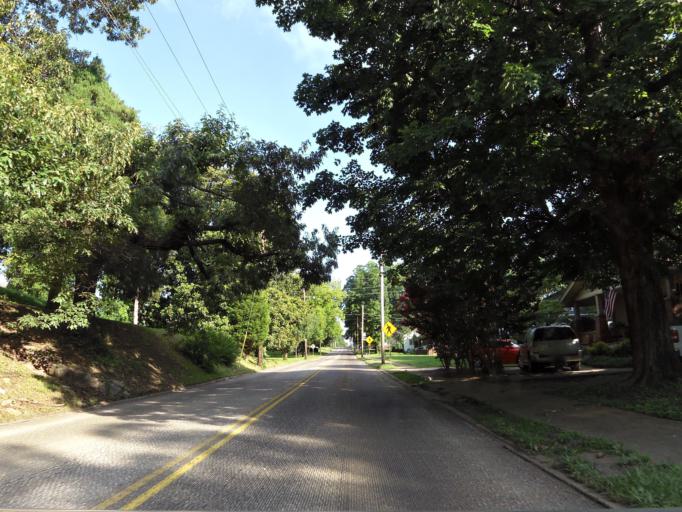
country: US
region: Tennessee
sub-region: Blount County
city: Maryville
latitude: 35.7517
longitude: -83.9670
